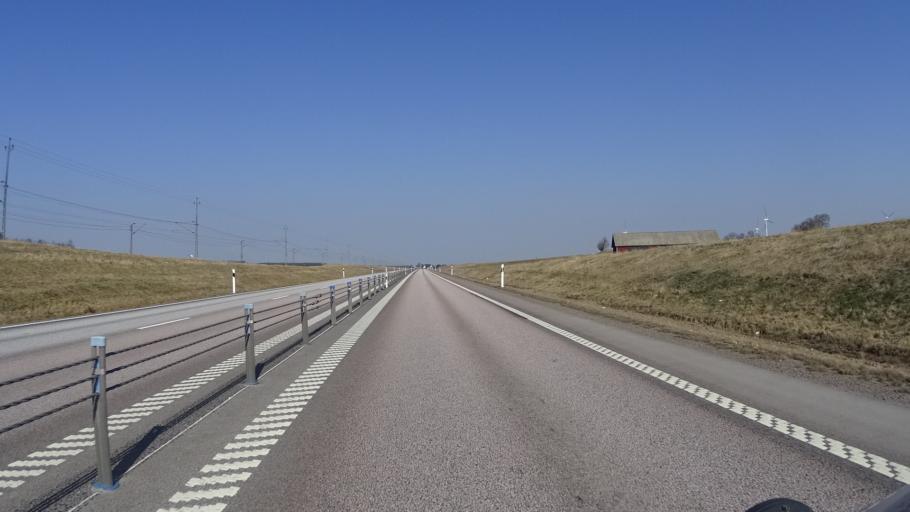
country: SE
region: OEstergoetland
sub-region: Motala Kommun
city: Stenstorp
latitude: 58.4342
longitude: 15.0611
